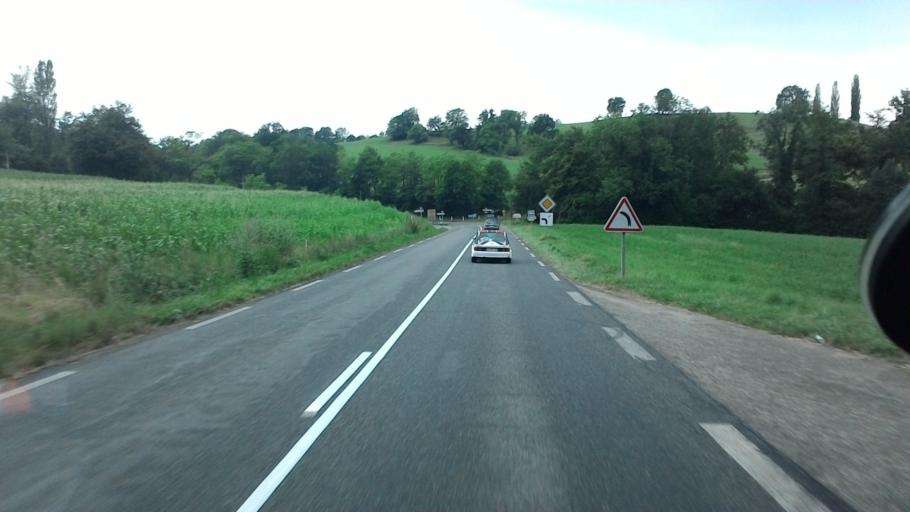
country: FR
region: Rhone-Alpes
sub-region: Departement de la Savoie
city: Yenne
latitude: 45.6962
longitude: 5.8039
